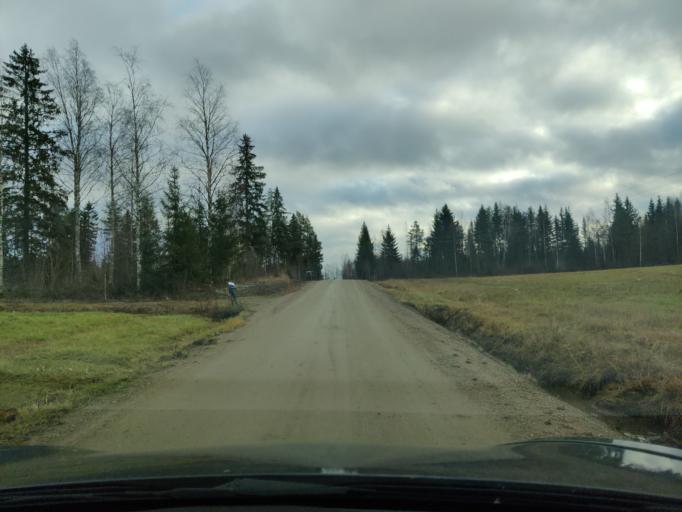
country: FI
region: Northern Savo
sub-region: Ylae-Savo
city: Kiuruvesi
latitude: 63.6386
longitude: 26.6446
